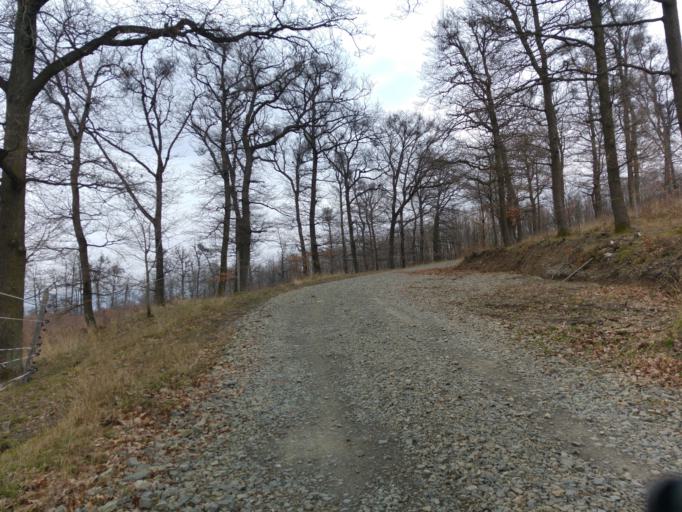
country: HU
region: Pest
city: Dunabogdany
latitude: 47.7587
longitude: 19.0378
